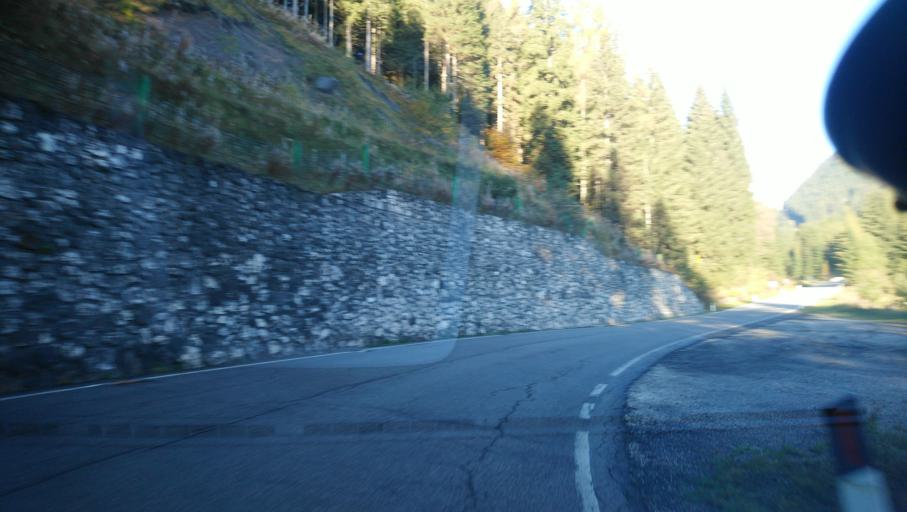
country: IT
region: Veneto
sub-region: Provincia di Belluno
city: Falcade Alto
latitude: 46.3589
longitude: 11.8482
